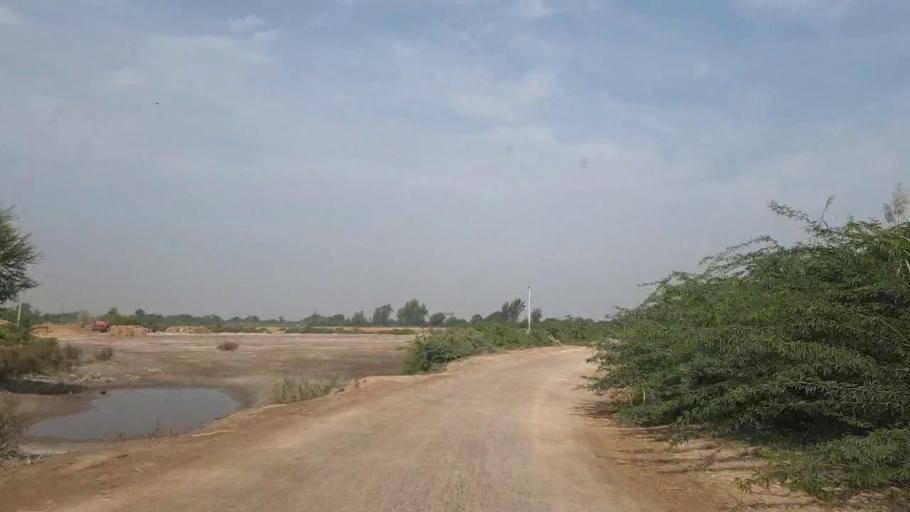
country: PK
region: Sindh
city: Tando Bago
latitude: 24.9217
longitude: 68.9912
